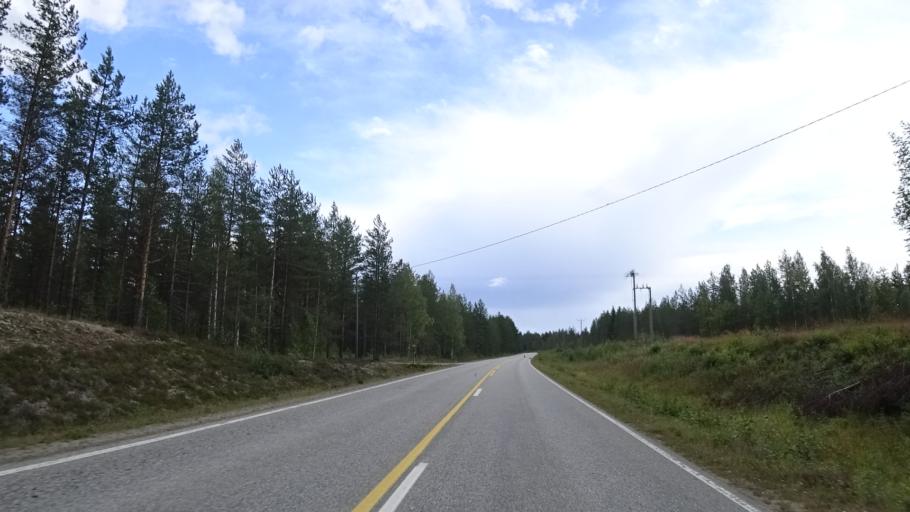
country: FI
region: North Karelia
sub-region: Joensuu
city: Ilomantsi
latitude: 62.6460
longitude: 31.0322
